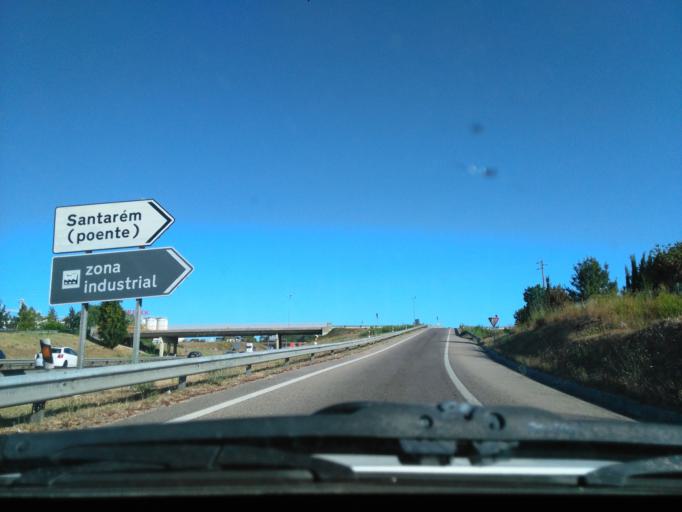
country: PT
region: Santarem
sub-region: Santarem
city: Santarem
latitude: 39.2588
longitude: -8.7032
